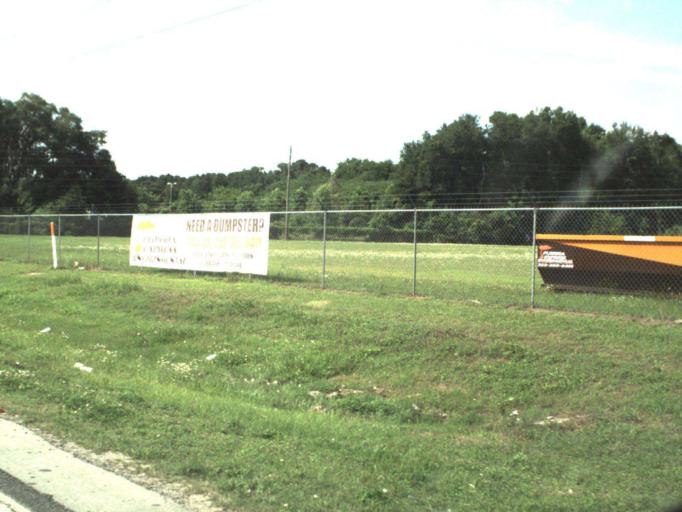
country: US
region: Florida
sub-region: Marion County
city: Ocala
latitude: 29.1373
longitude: -82.1089
